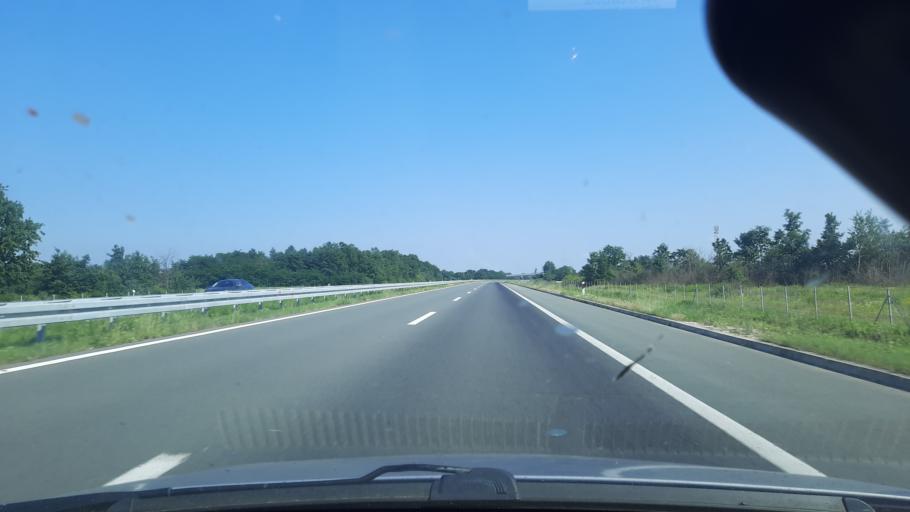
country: RS
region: Central Serbia
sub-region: Kolubarski Okrug
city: Lajkovac
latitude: 44.3843
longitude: 20.1106
